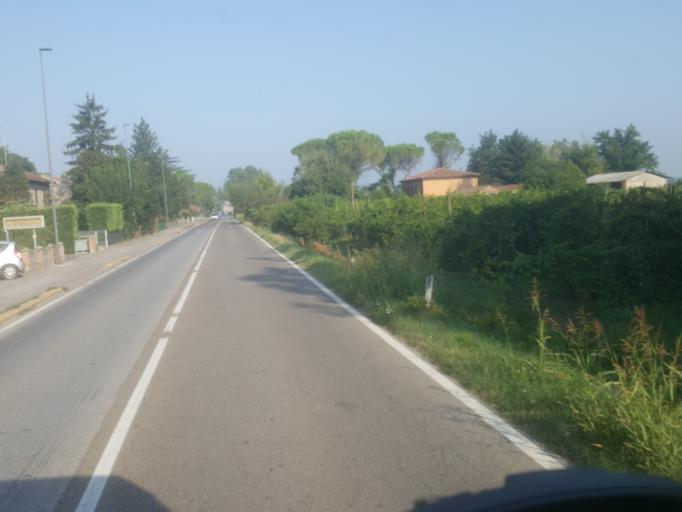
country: IT
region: Emilia-Romagna
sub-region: Provincia di Ravenna
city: Mezzano
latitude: 44.4617
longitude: 12.0956
